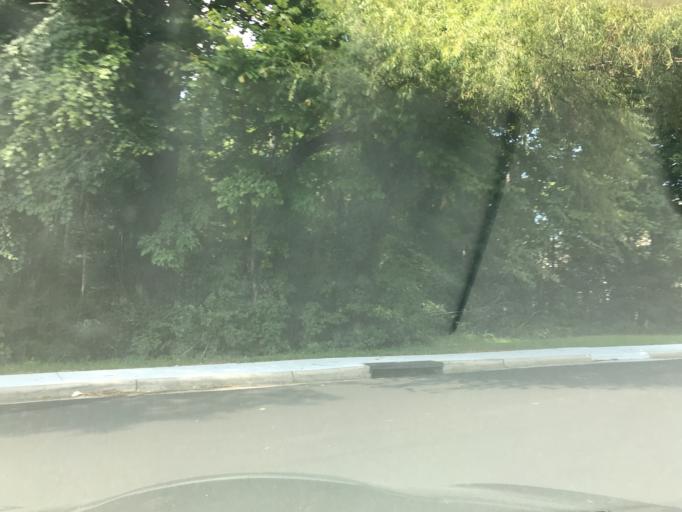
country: US
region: North Carolina
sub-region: Durham County
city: Durham
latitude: 35.9033
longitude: -78.8981
